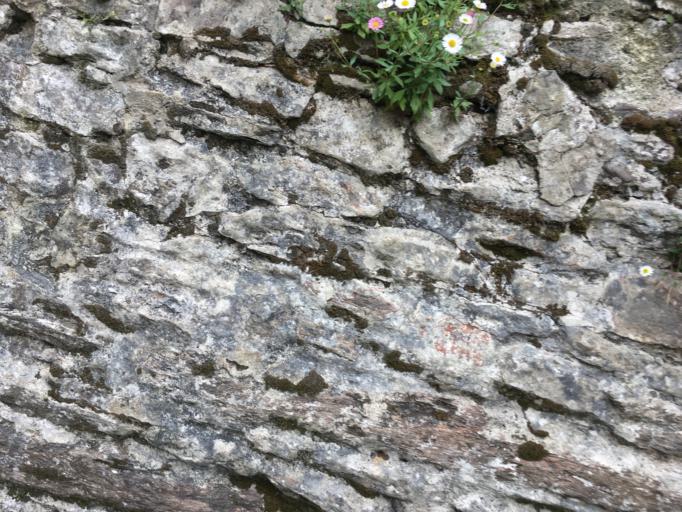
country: GB
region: England
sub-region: Devon
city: Dartmouth
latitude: 50.3477
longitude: -3.5785
